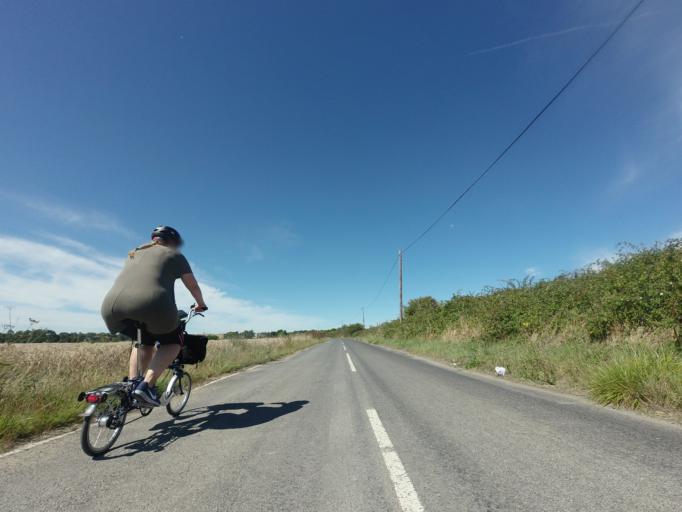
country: GB
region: England
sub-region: Kent
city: Sandwich
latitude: 51.3245
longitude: 1.3479
